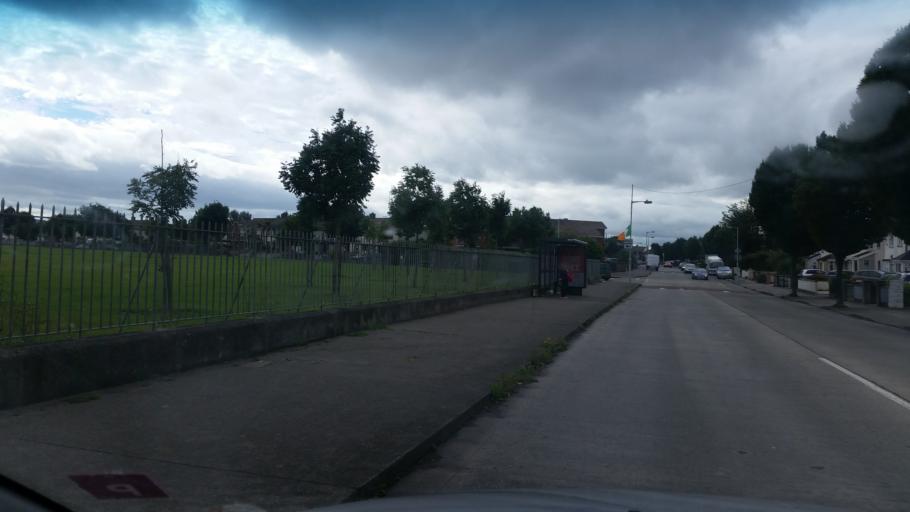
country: IE
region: Leinster
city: Raheny
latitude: 53.3939
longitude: -6.1785
